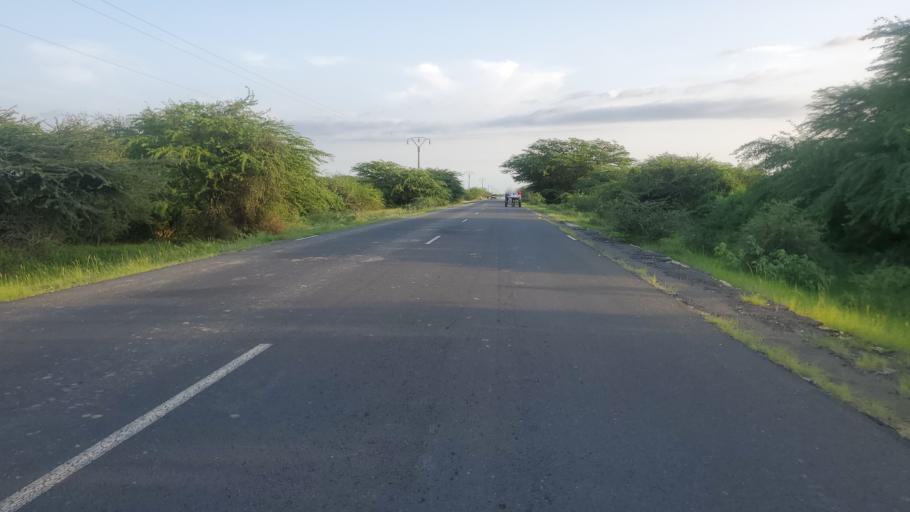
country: SN
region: Saint-Louis
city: Saint-Louis
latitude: 16.1890
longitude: -16.4093
